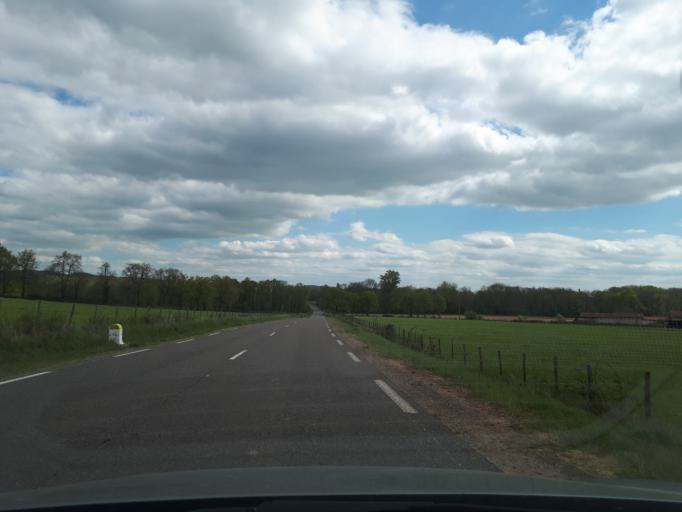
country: FR
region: Rhone-Alpes
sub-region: Departement de la Loire
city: Civens
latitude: 45.7496
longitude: 4.2725
